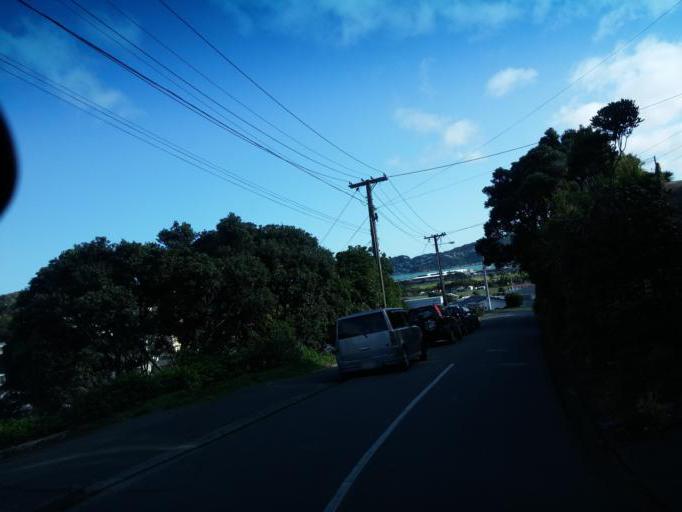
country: NZ
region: Wellington
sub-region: Wellington City
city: Wellington
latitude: -41.3236
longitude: 174.8261
